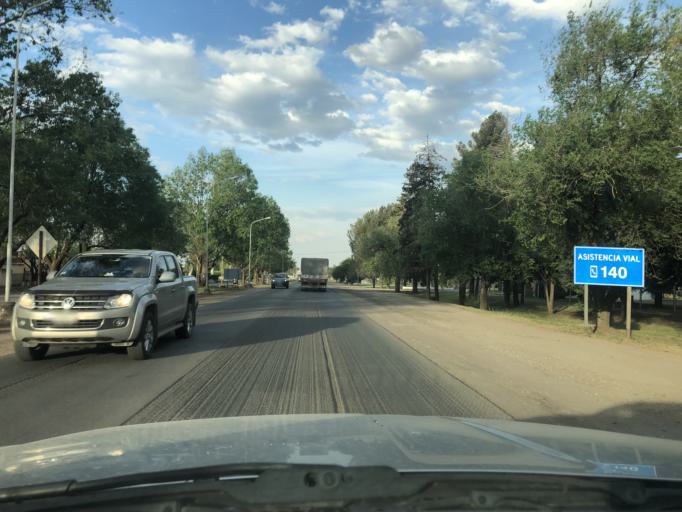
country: AR
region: Cordoba
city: Jesus Maria
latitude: -30.9898
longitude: -64.0952
